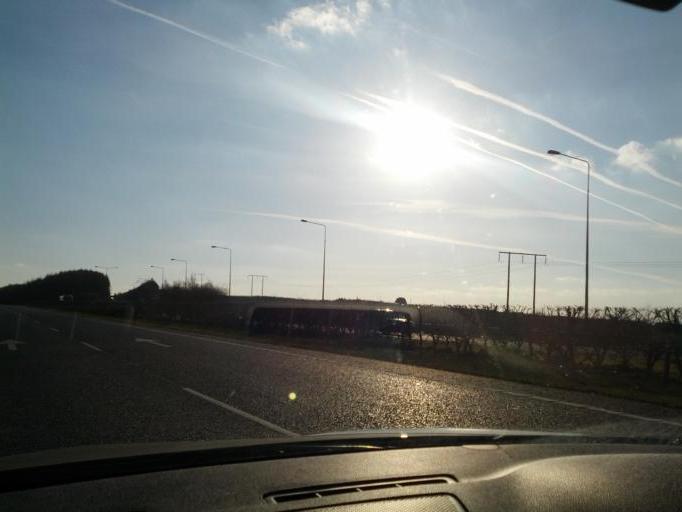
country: IE
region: Leinster
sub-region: Laois
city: Portlaoise
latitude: 53.0543
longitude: -7.2345
